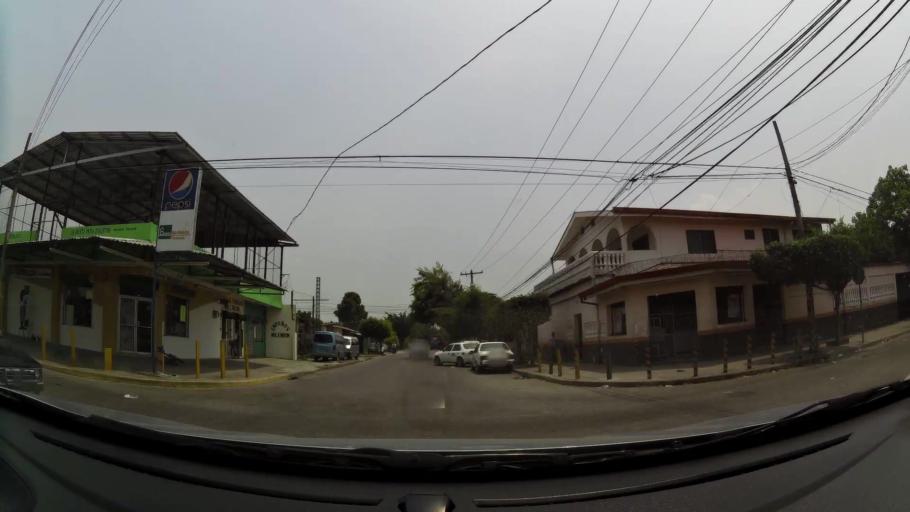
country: HN
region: Cortes
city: San Pedro Sula
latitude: 15.4925
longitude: -88.0113
